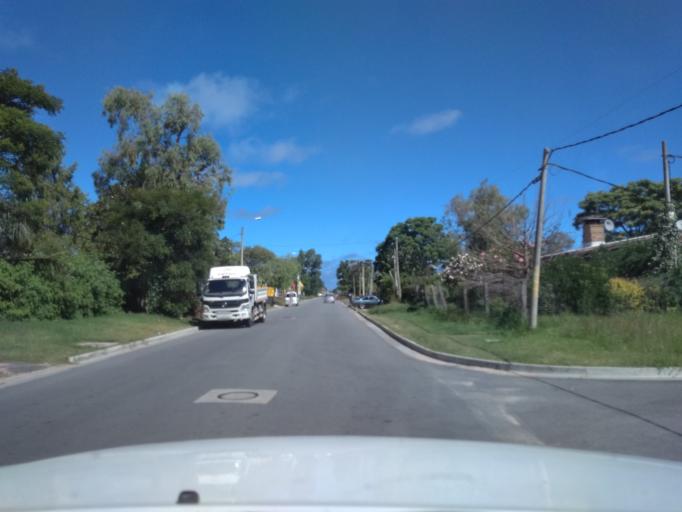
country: UY
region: Canelones
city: Colonia Nicolich
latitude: -34.8246
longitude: -55.9714
